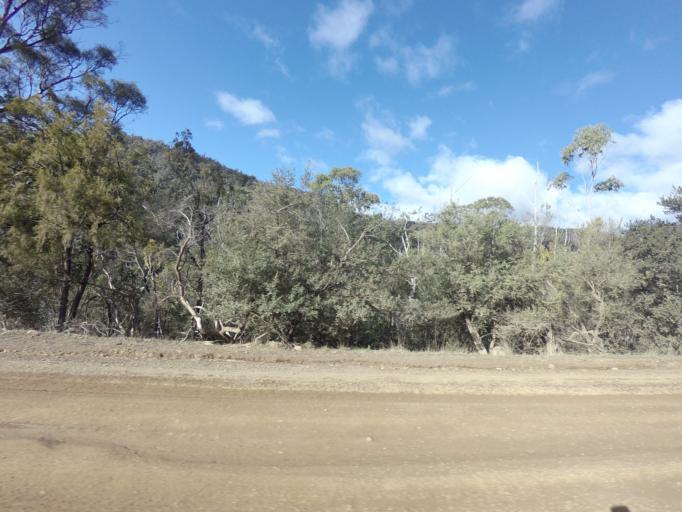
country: AU
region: Tasmania
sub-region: Derwent Valley
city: New Norfolk
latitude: -42.8185
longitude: 147.1277
